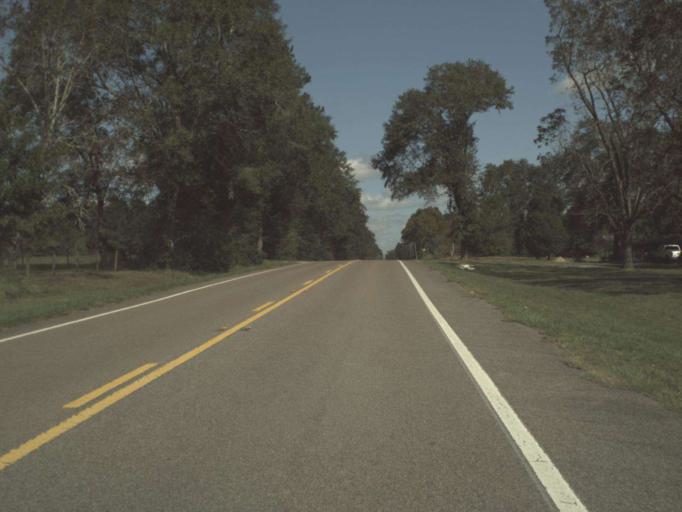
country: US
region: Alabama
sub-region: Geneva County
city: Samson
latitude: 30.9753
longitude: -86.1350
